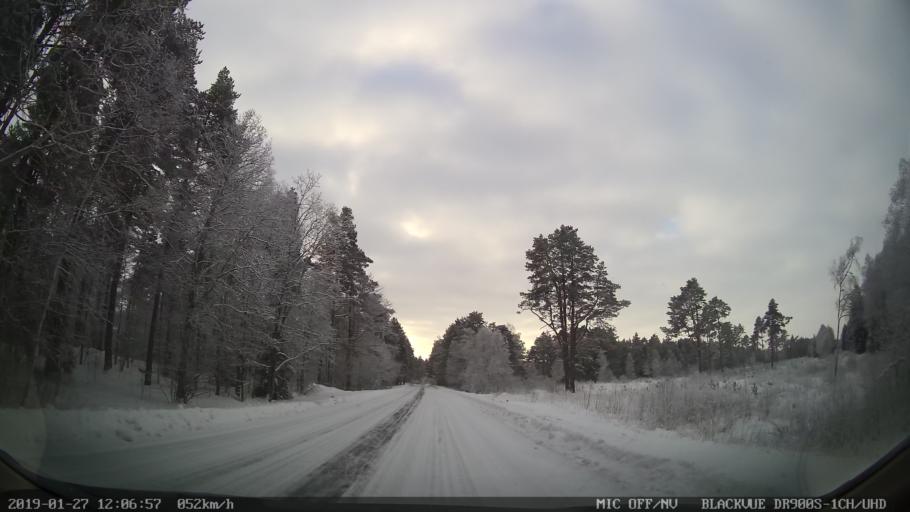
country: EE
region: Harju
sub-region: Raasiku vald
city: Raasiku
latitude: 59.4675
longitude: 25.2401
